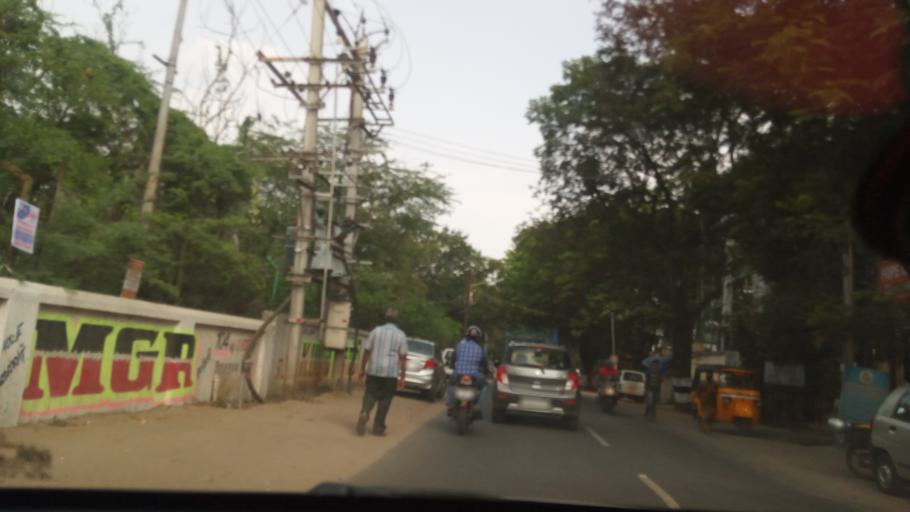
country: IN
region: Tamil Nadu
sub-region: Coimbatore
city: Coimbatore
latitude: 11.0154
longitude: 76.9525
